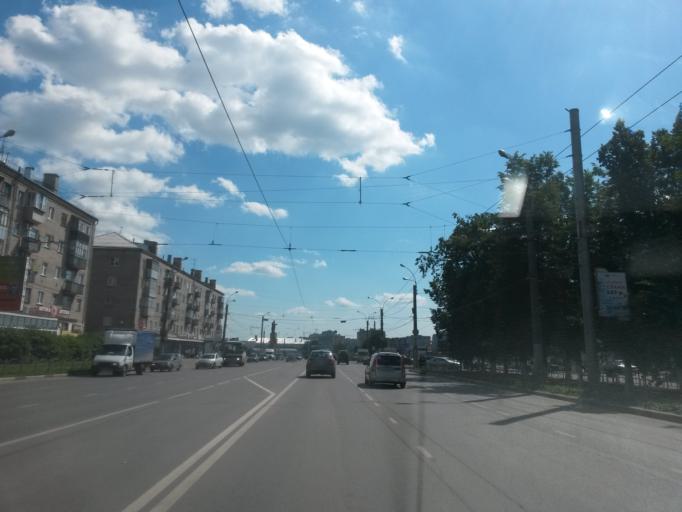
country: RU
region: Ivanovo
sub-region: Gorod Ivanovo
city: Ivanovo
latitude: 57.0089
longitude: 40.9893
